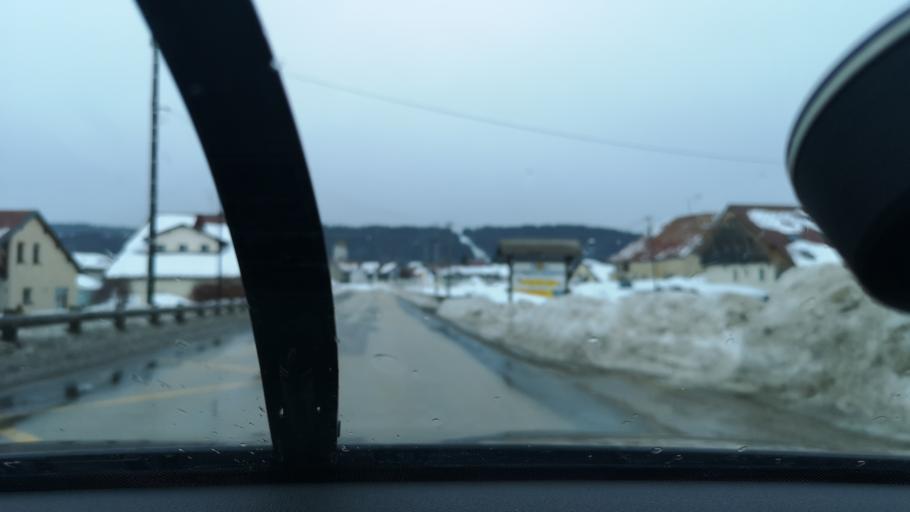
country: FR
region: Franche-Comte
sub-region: Departement du Doubs
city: Les Fourgs
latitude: 46.8392
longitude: 6.3960
